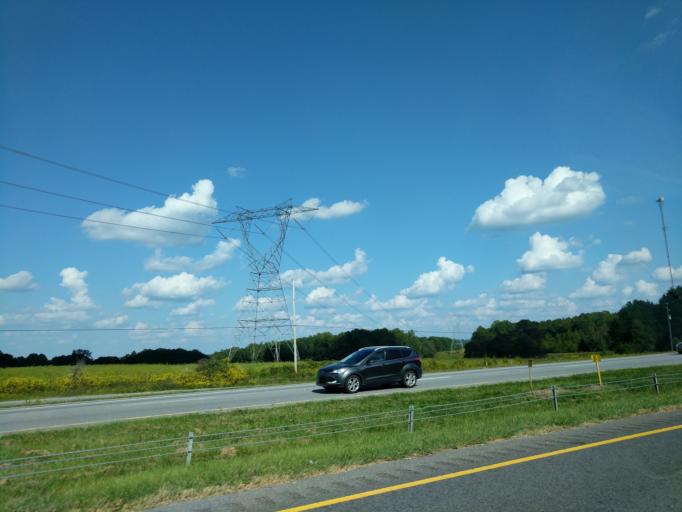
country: US
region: South Carolina
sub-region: Greenville County
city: Fountain Inn
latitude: 34.6525
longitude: -82.1600
